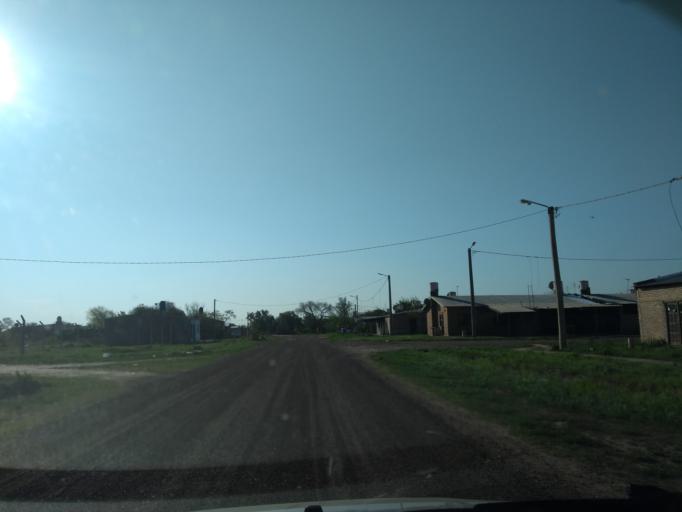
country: AR
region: Chaco
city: Fontana
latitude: -27.4150
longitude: -59.0559
